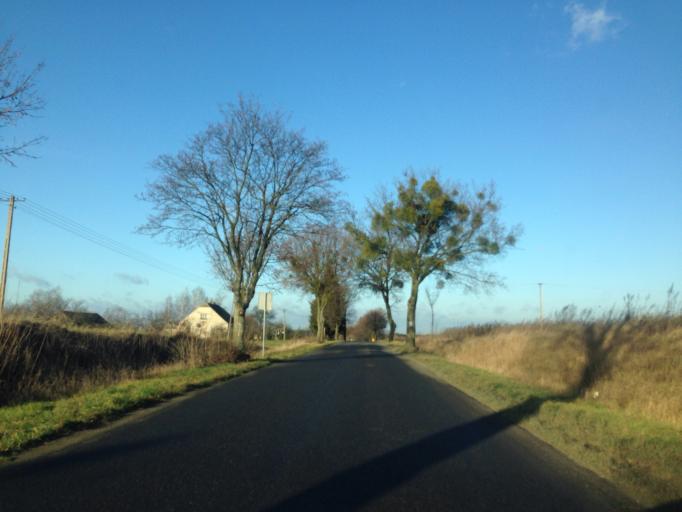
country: PL
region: Kujawsko-Pomorskie
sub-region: Powiat brodnicki
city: Jablonowo Pomorskie
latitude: 53.4093
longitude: 19.1385
